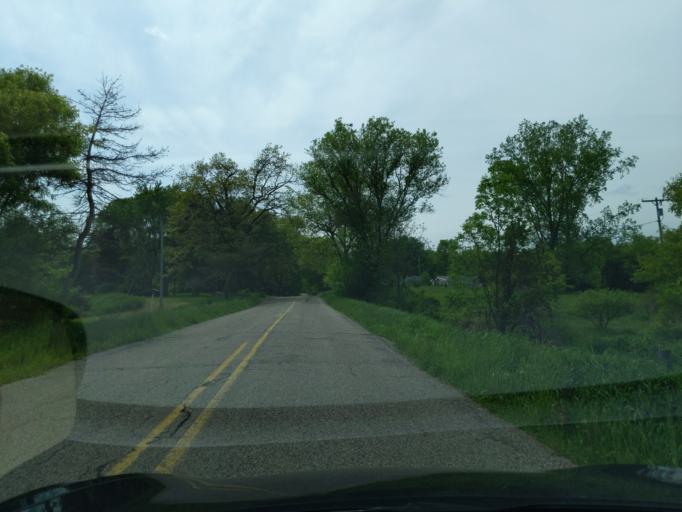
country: US
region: Michigan
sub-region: Ingham County
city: Leslie
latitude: 42.4319
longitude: -84.3485
